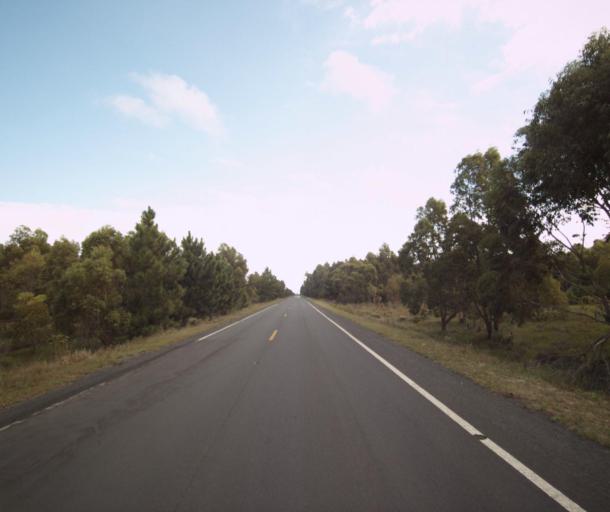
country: BR
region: Rio Grande do Sul
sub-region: Tapes
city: Tapes
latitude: -31.4287
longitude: -51.1870
